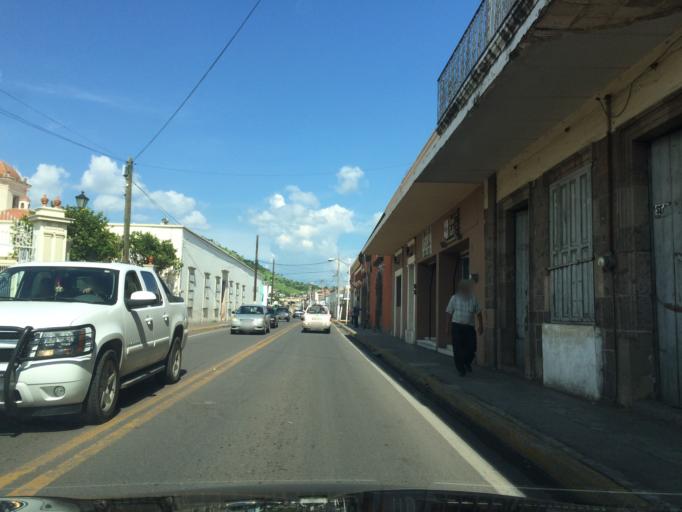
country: MX
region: Nayarit
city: Ixtlan del Rio
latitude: 21.0351
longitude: -104.3687
